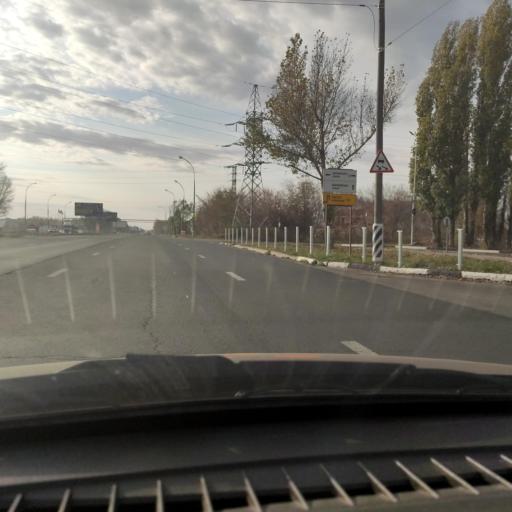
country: RU
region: Samara
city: Tol'yatti
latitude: 53.5461
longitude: 49.2857
